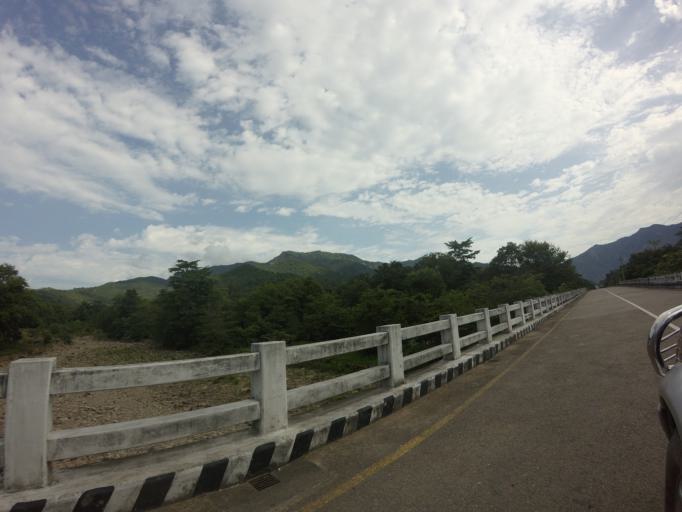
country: NP
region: Far Western
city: Tikapur
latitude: 28.6208
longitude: 81.2432
